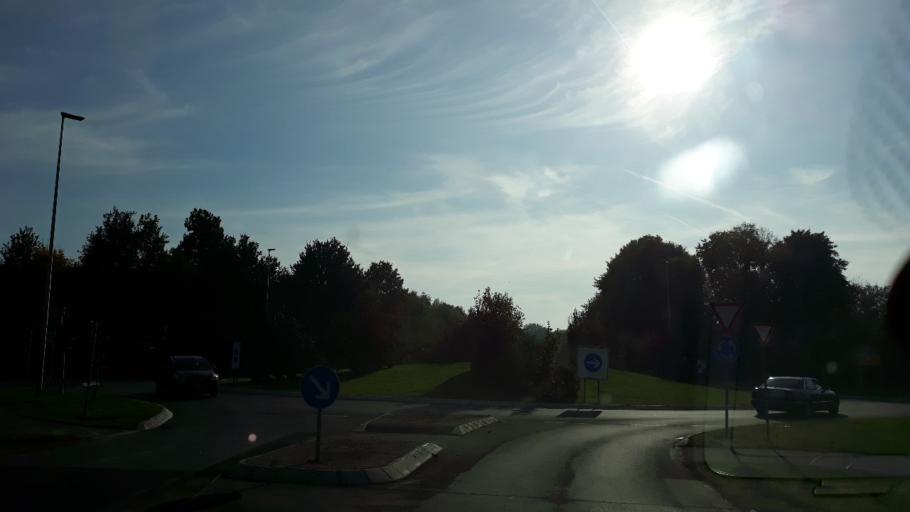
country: DE
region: Schleswig-Holstein
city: Schleswig
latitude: 54.5310
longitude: 9.5738
